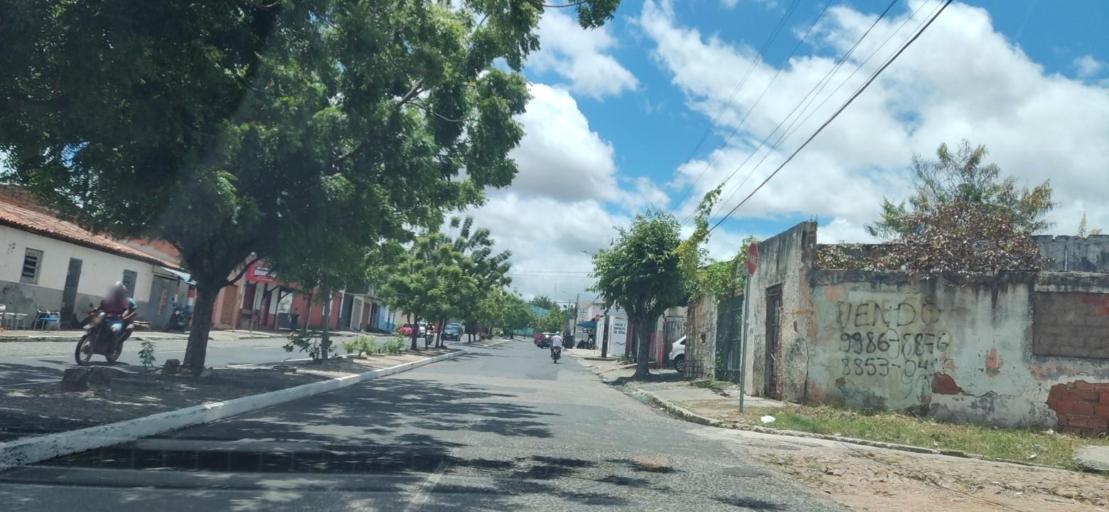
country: BR
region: Piaui
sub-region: Teresina
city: Teresina
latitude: -5.1467
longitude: -42.7798
